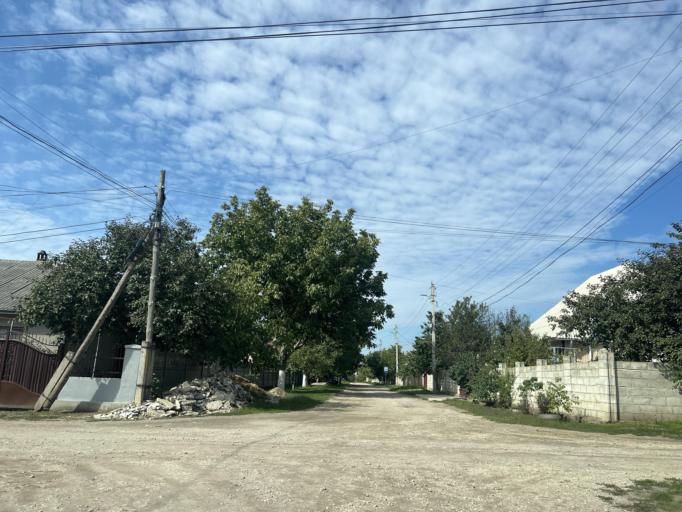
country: MD
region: Ungheni
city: Ungheni
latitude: 47.2024
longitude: 27.8156
